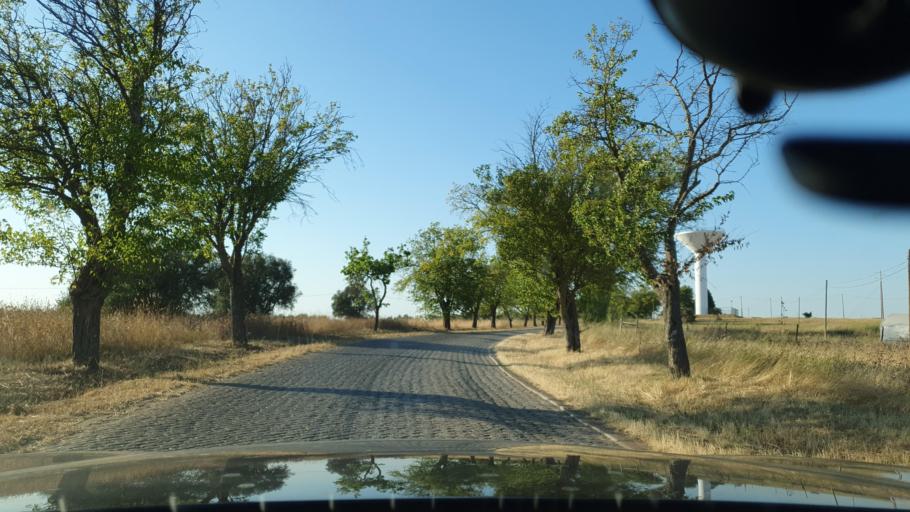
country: PT
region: Portalegre
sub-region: Fronteira
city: Fronteira
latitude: 38.9417
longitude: -7.6770
